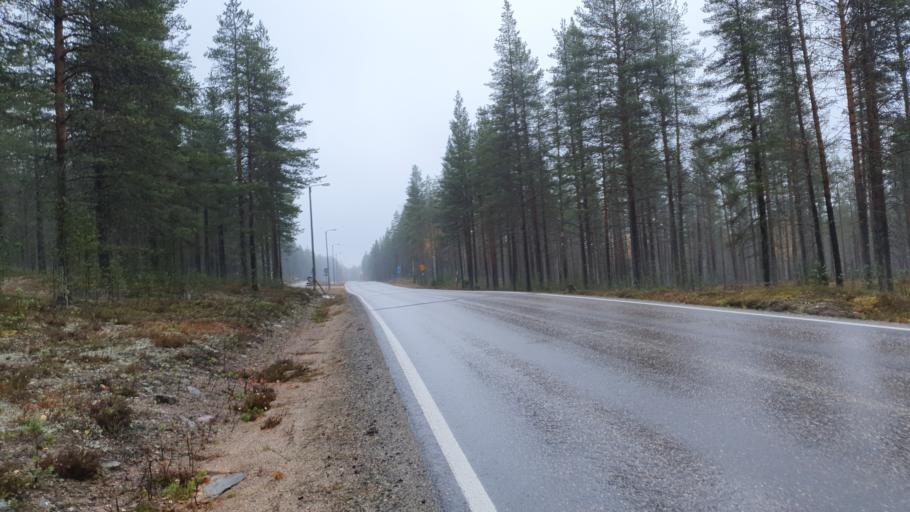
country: FI
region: Lapland
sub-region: Tunturi-Lappi
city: Kolari
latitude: 67.5963
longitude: 24.1173
